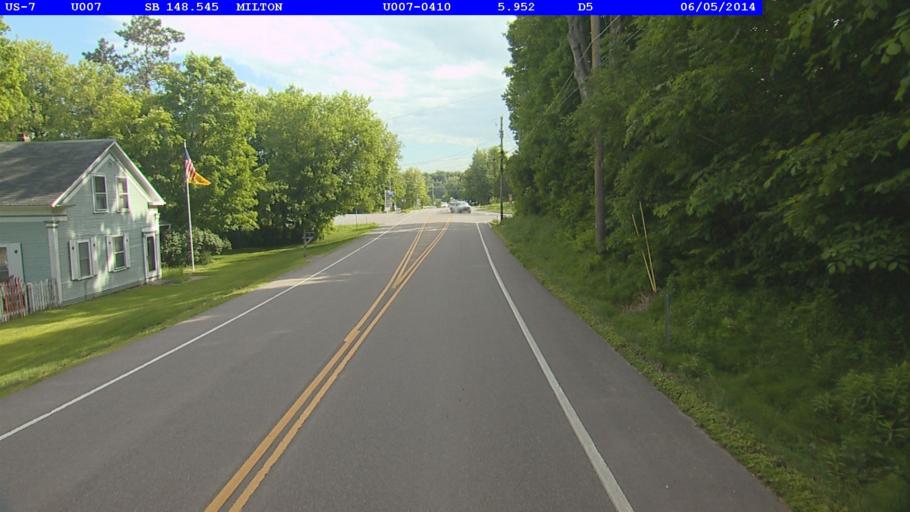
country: US
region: Vermont
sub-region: Chittenden County
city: Milton
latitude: 44.6524
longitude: -73.1147
